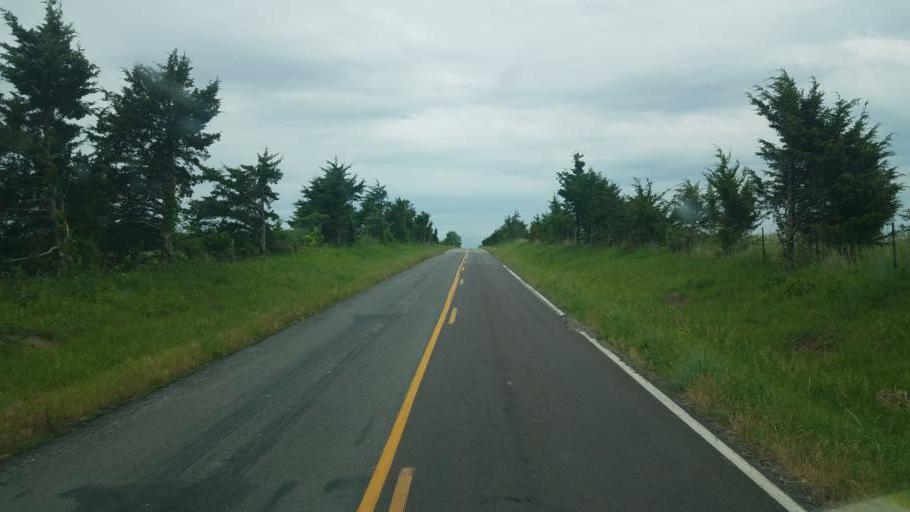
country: US
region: Missouri
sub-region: Moniteau County
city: California
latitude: 38.7049
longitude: -92.6347
